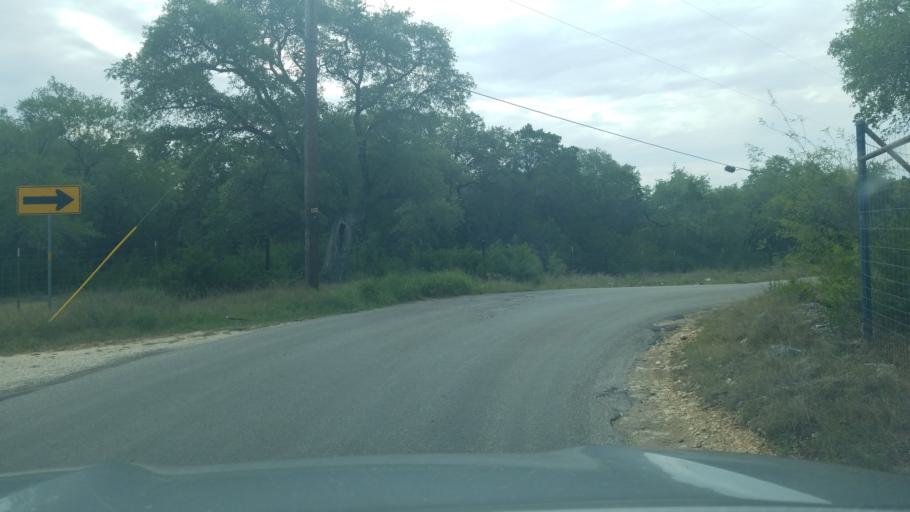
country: US
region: Texas
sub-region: Comal County
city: Bulverde
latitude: 29.7646
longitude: -98.4090
